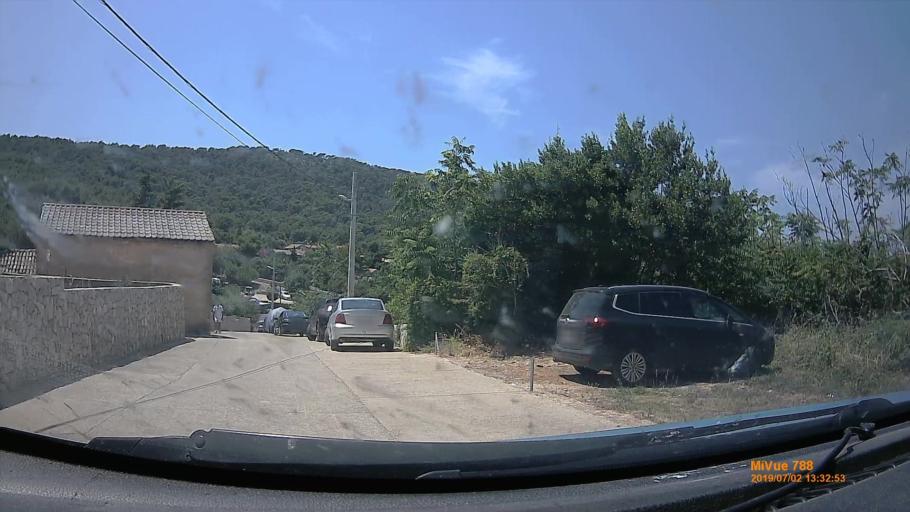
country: HR
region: Primorsko-Goranska
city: Mali Losinj
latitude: 44.5147
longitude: 14.5085
